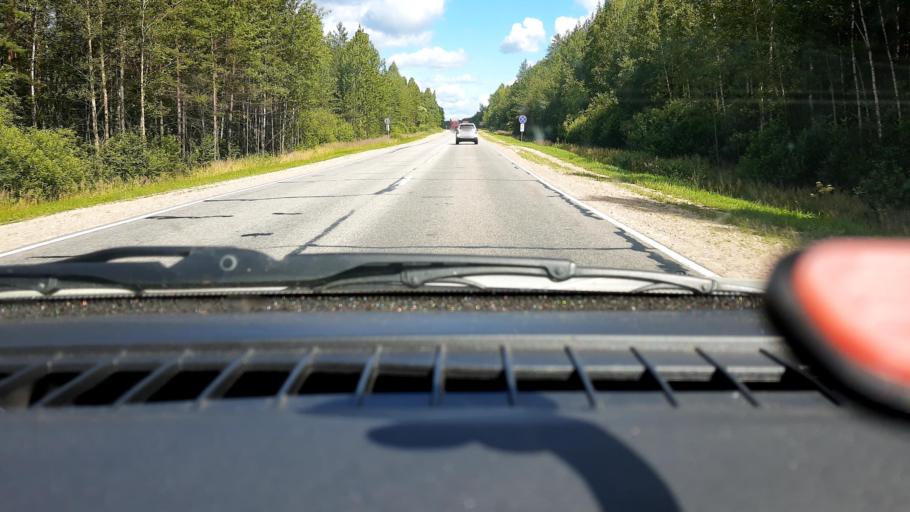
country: RU
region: Nizjnij Novgorod
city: Arzamas
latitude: 55.4076
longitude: 43.9152
